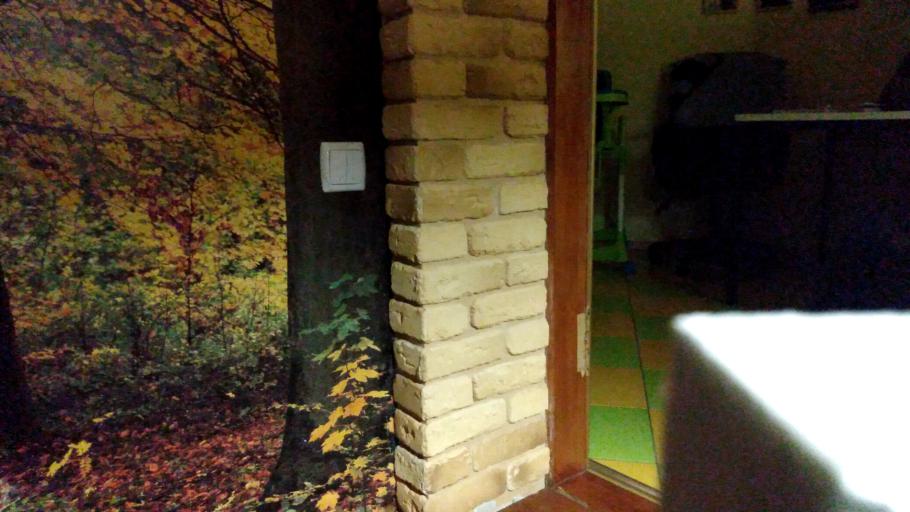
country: RU
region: Vologda
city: Lipin Bor
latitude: 60.9125
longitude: 37.9925
